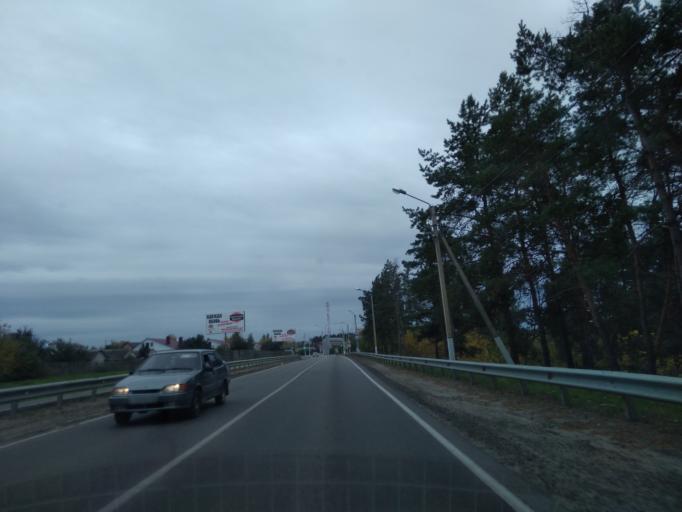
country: RU
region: Lipetsk
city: Zadonsk
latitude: 52.3848
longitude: 38.9372
